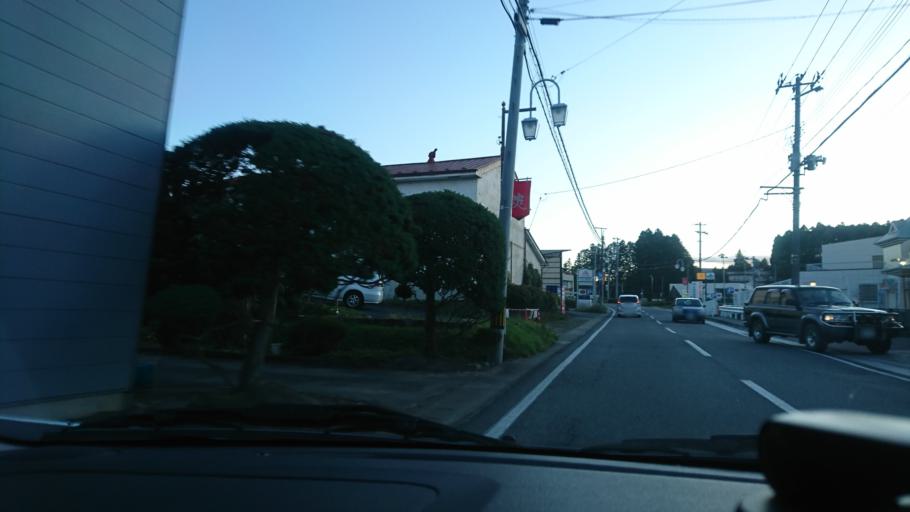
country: JP
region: Iwate
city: Ichinoseki
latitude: 38.8598
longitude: 141.3493
